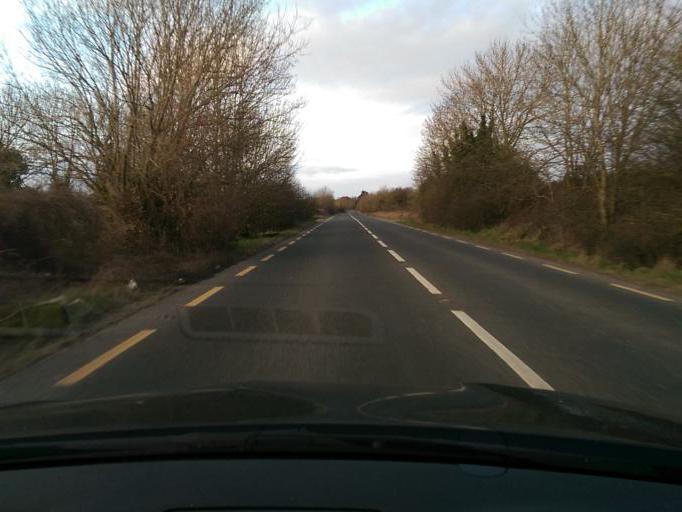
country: IE
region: Munster
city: Nenagh Bridge
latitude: 52.8879
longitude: -8.1918
